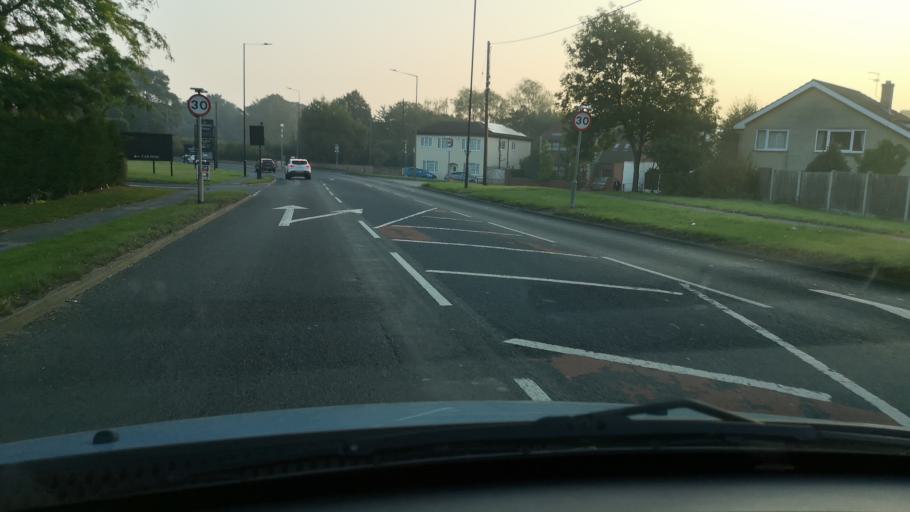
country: GB
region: England
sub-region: Doncaster
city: Hatfield
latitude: 53.5718
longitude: -1.0082
